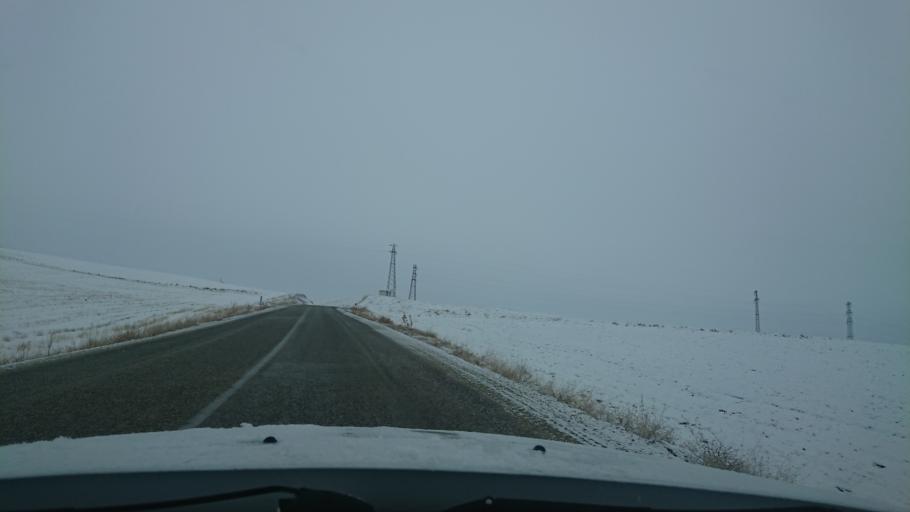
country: TR
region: Aksaray
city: Agacoren
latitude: 38.7650
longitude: 33.8713
